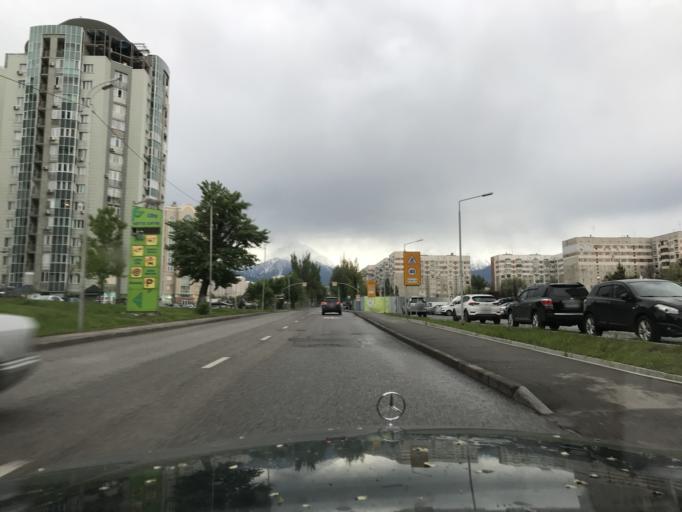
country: KZ
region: Almaty Qalasy
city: Almaty
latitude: 43.2168
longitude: 76.8812
